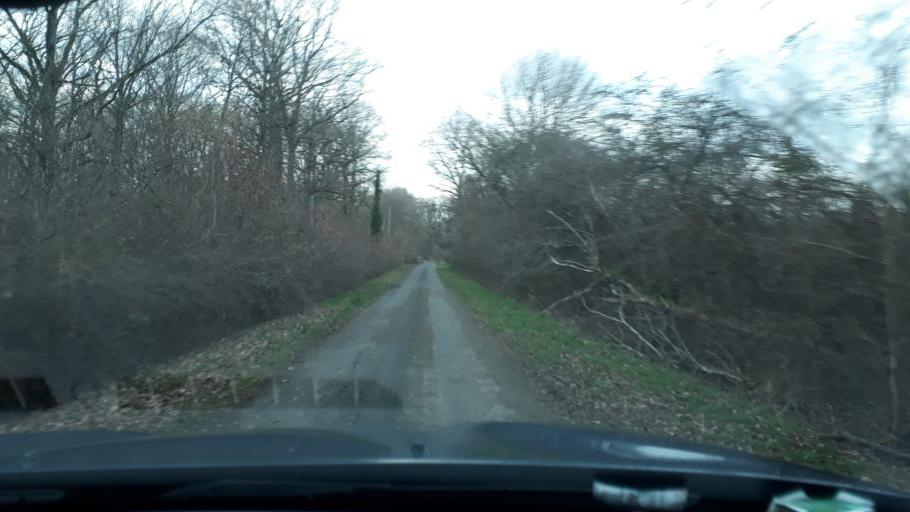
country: FR
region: Centre
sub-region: Departement du Loiret
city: Chilleurs-aux-Bois
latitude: 48.0547
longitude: 2.1576
